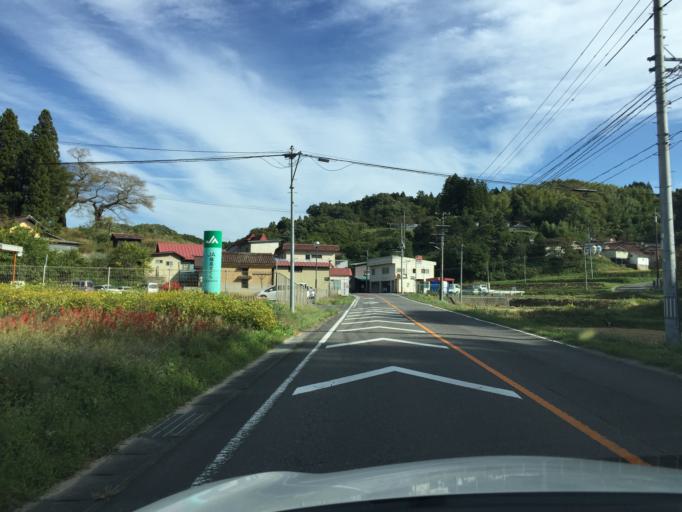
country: JP
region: Fukushima
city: Miharu
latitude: 37.3610
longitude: 140.4665
